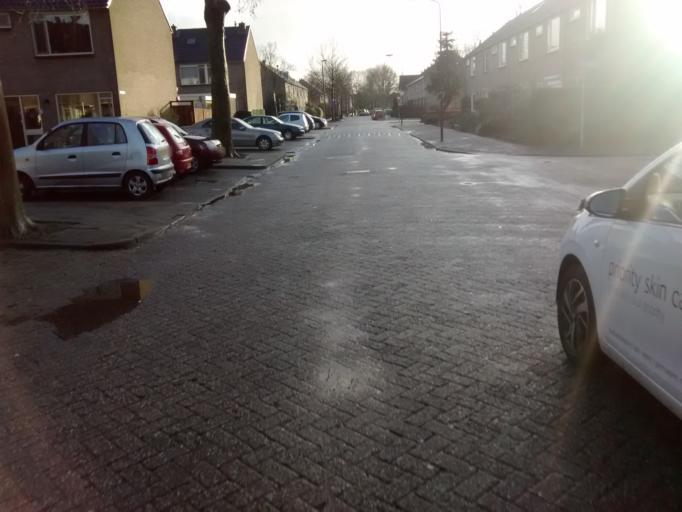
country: NL
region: Utrecht
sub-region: Gemeente Vianen
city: Vianen
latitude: 52.0098
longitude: 5.0911
